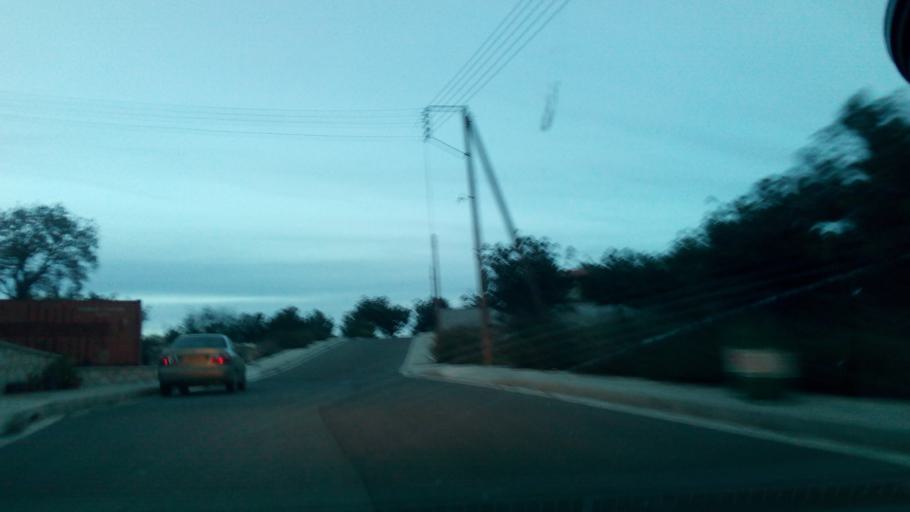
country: CY
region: Pafos
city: Polis
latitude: 35.0004
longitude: 32.5148
